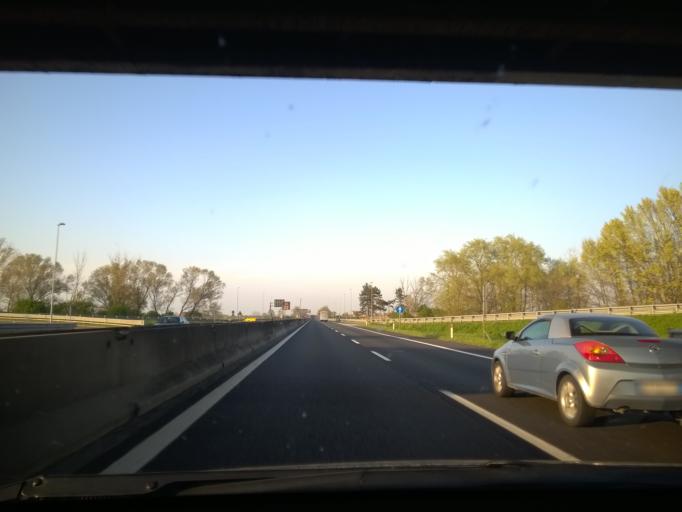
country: IT
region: Emilia-Romagna
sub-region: Provincia di Bologna
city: Altedo
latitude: 44.6886
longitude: 11.4804
